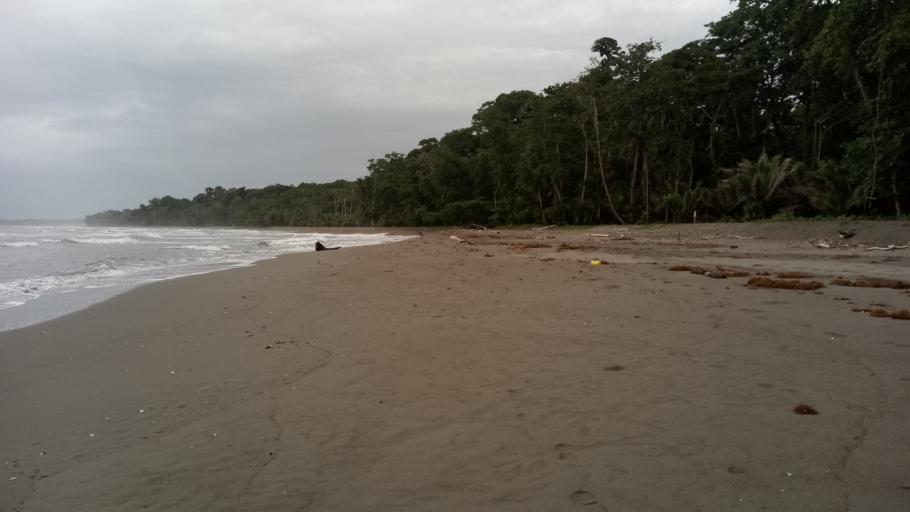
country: CR
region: Limon
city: Sixaola
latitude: 9.6171
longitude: -82.6204
